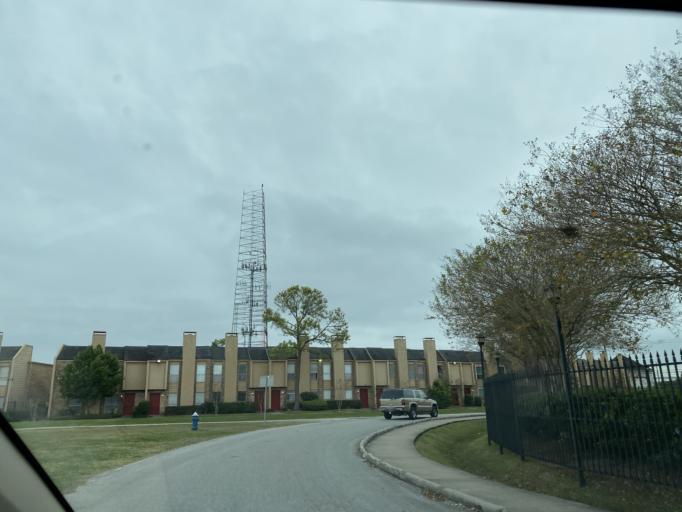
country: US
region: Texas
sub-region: Harris County
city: Piney Point Village
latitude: 29.7306
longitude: -95.4920
